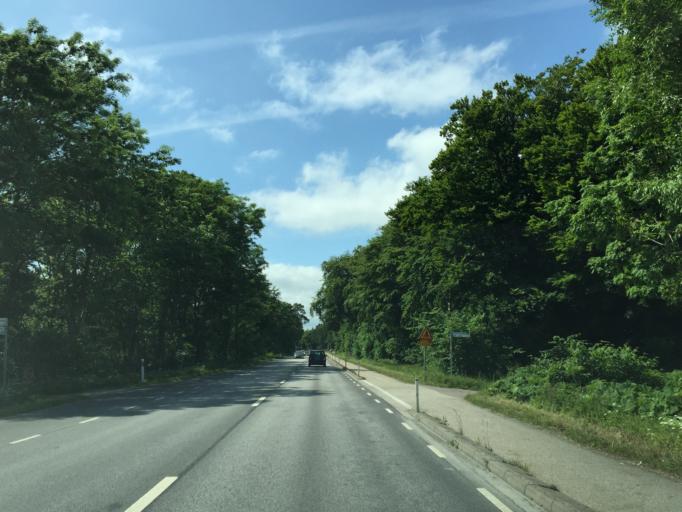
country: SE
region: Skane
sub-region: Ystads Kommun
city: Kopingebro
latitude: 55.4358
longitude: 13.9196
